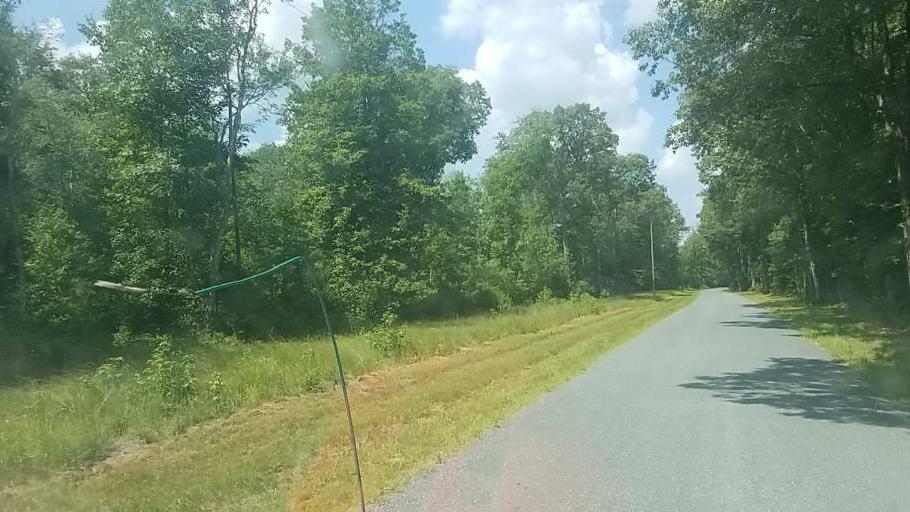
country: US
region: Maryland
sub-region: Worcester County
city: Snow Hill
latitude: 38.2478
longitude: -75.4177
